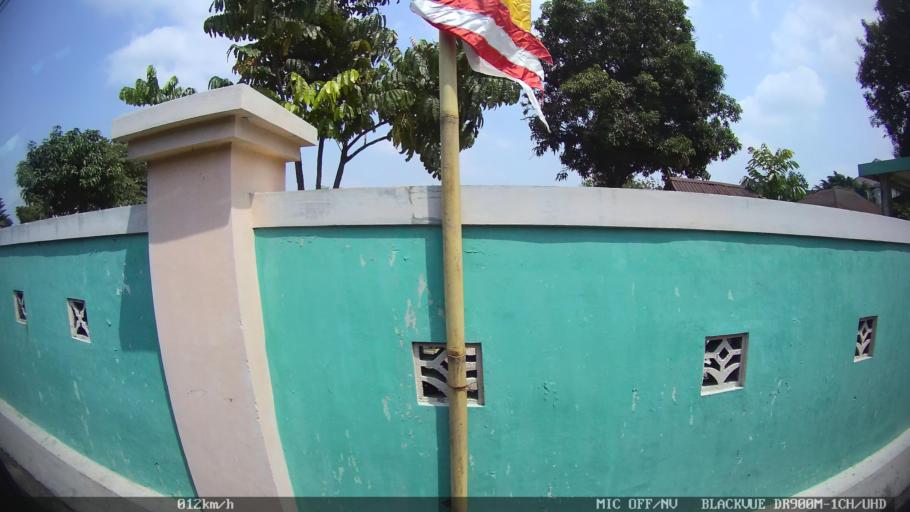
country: ID
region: Daerah Istimewa Yogyakarta
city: Yogyakarta
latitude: -7.8024
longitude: 110.3845
